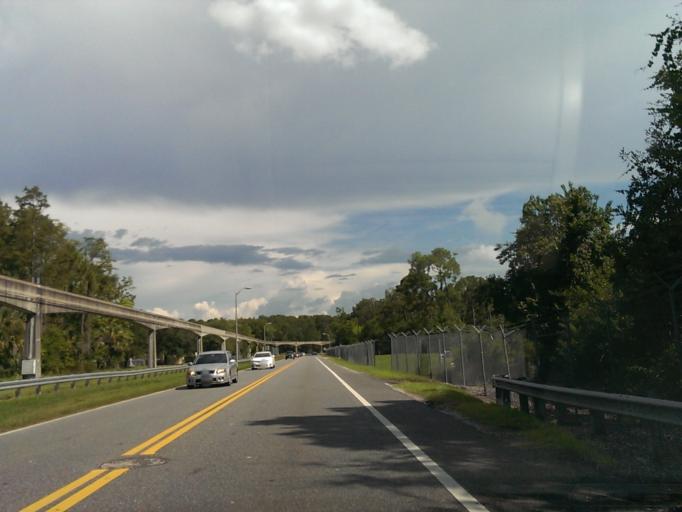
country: US
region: Florida
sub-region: Orange County
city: Bay Hill
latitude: 28.4229
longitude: -81.5779
